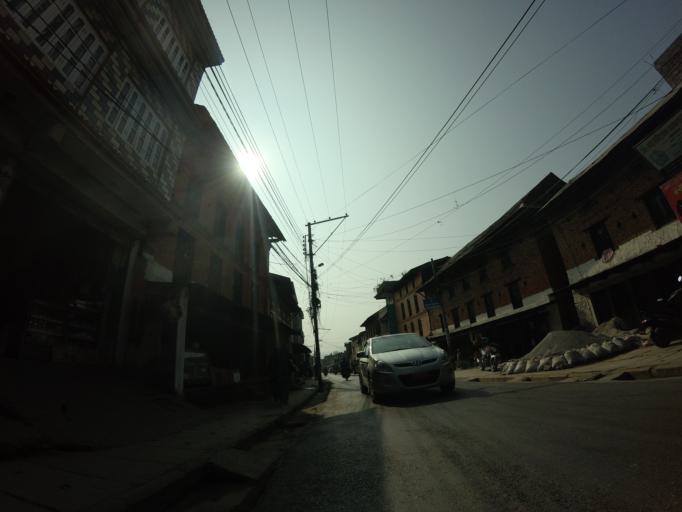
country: NP
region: Western Region
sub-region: Gandaki Zone
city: Pokhara
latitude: 28.2319
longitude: 83.9852
